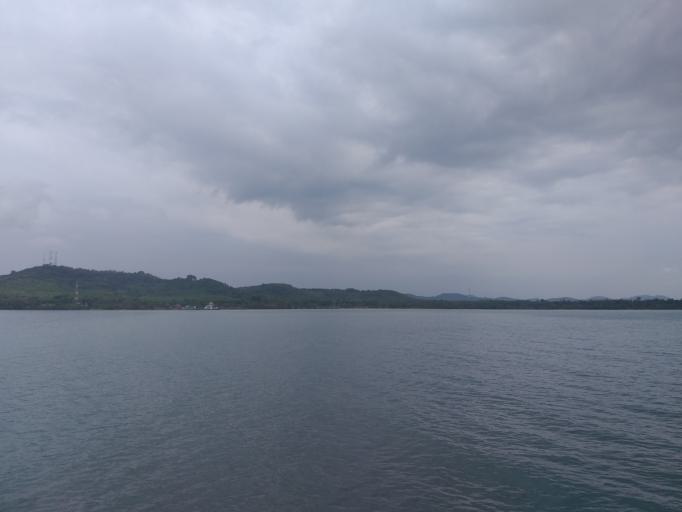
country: TH
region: Trat
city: Laem Ngop
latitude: 12.1745
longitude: 102.2989
